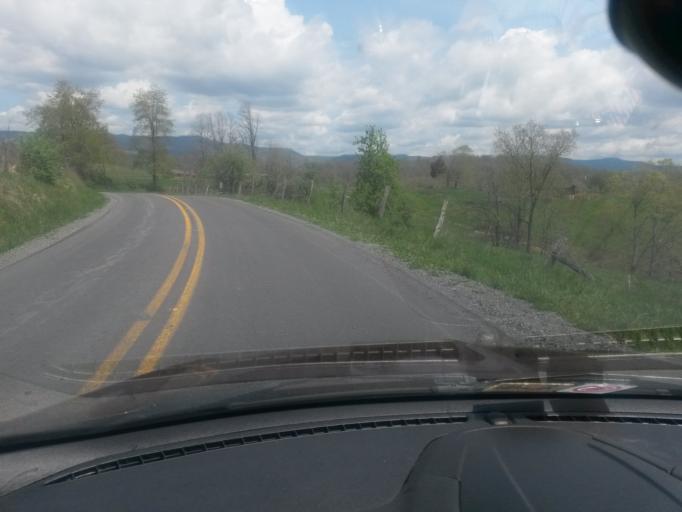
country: US
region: West Virginia
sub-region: Pocahontas County
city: Marlinton
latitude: 38.1032
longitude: -80.2256
